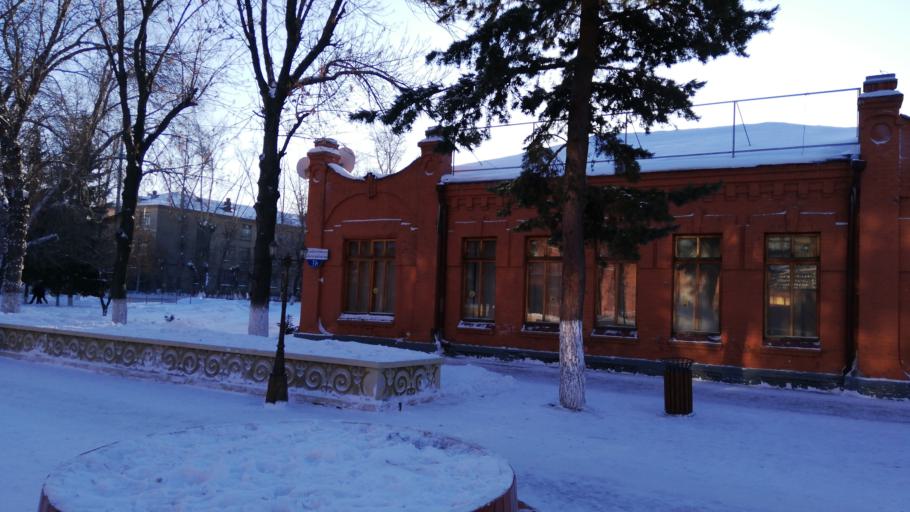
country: KZ
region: Soltustik Qazaqstan
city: Petropavlovsk
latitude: 54.8649
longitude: 69.1366
